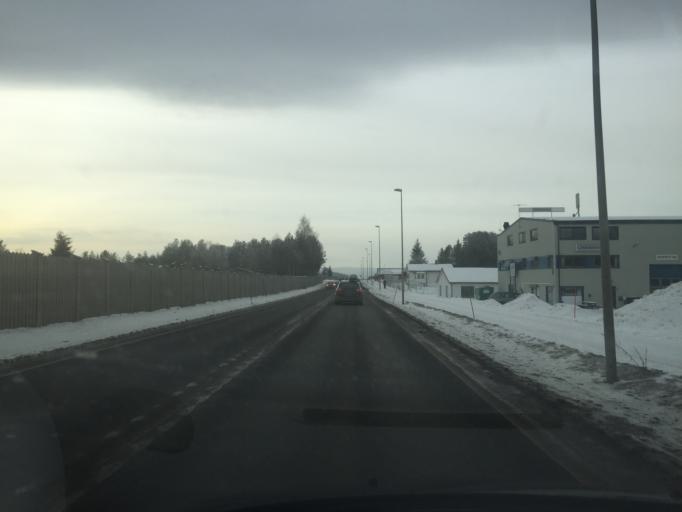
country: NO
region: Hedmark
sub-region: Elverum
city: Elverum
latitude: 60.9007
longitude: 11.5956
